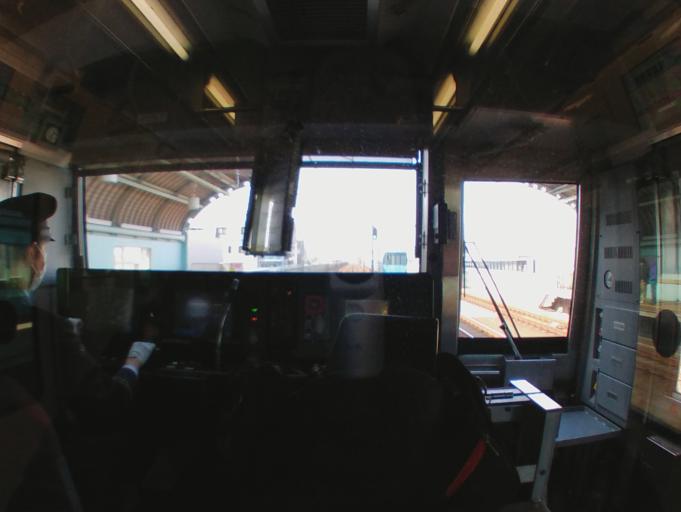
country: JP
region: Tokyo
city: Chofugaoka
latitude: 35.6441
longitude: 139.6124
